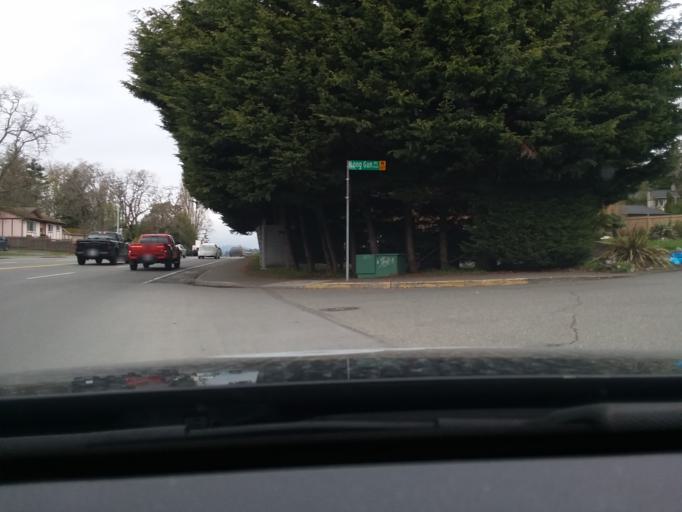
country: CA
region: British Columbia
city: Oak Bay
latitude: 48.4689
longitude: -123.3412
